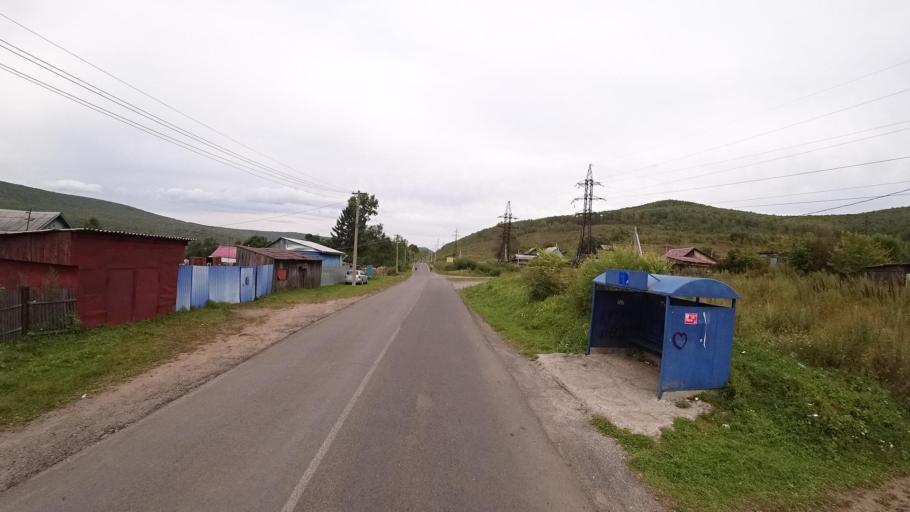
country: RU
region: Jewish Autonomous Oblast
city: Khingansk
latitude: 49.0373
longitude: 131.0589
